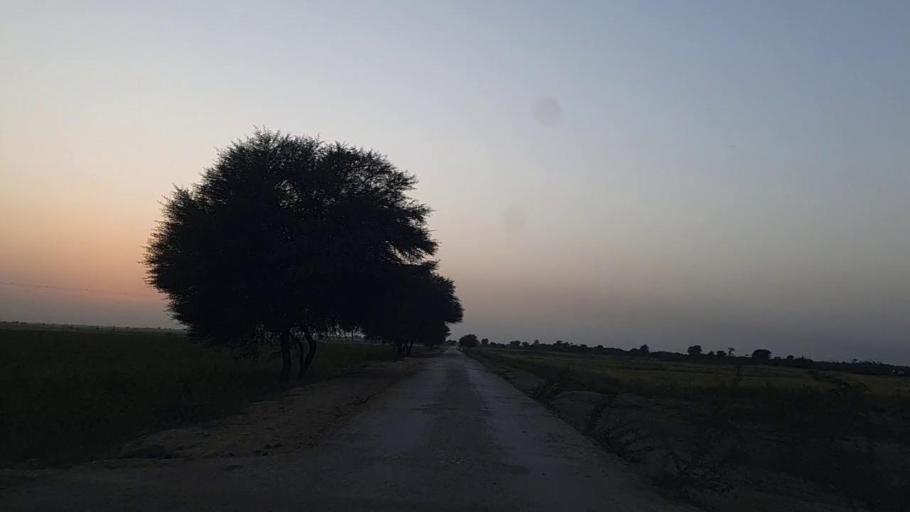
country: PK
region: Sindh
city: Naukot
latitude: 24.7496
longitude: 69.3090
